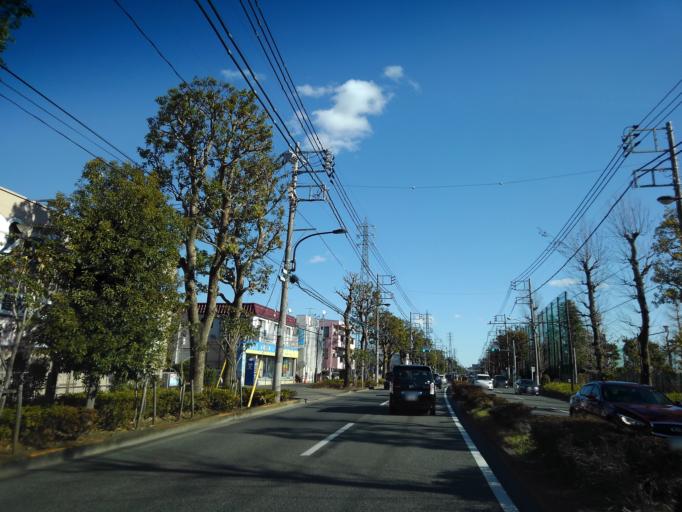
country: JP
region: Tokyo
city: Kokubunji
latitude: 35.6886
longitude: 139.4815
